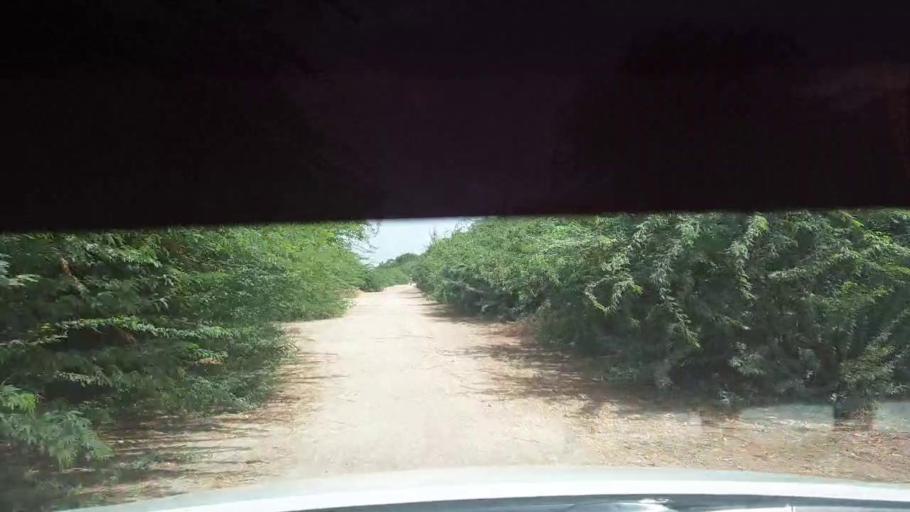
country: PK
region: Sindh
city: Kadhan
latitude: 24.5107
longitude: 68.9761
